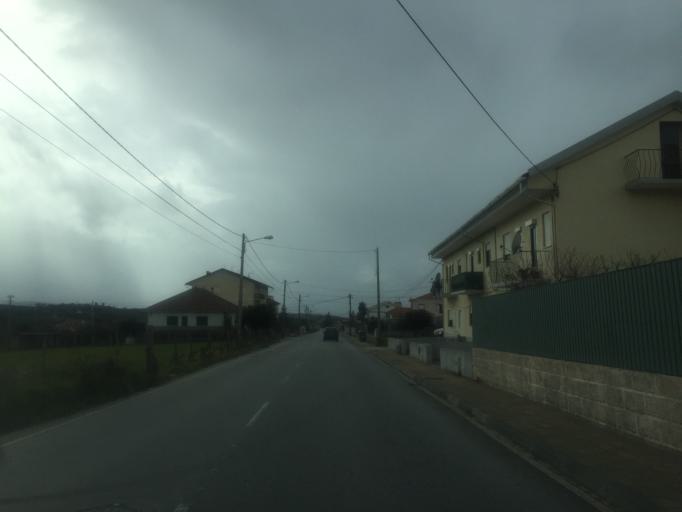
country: PT
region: Guarda
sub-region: Seia
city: Seia
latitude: 40.4023
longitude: -7.7275
